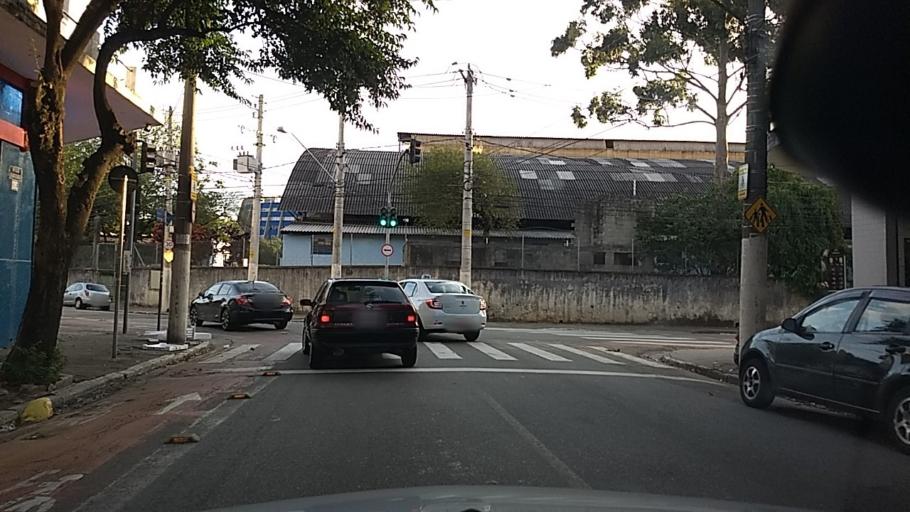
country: BR
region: Sao Paulo
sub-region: Sao Paulo
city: Sao Paulo
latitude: -23.5273
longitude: -46.6220
